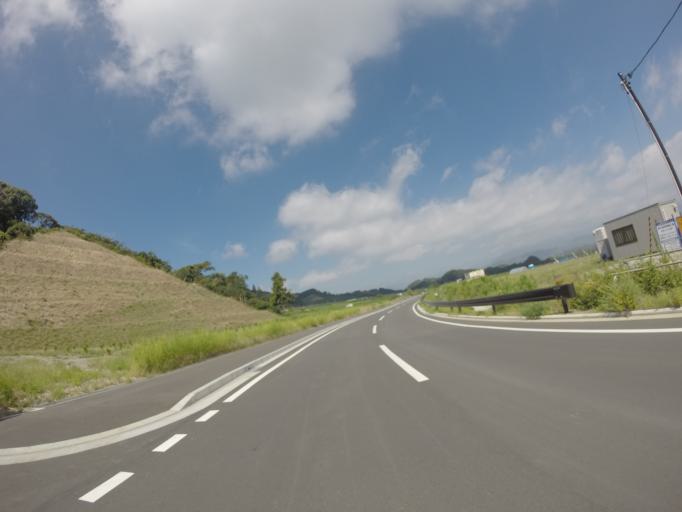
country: JP
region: Shizuoka
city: Shizuoka-shi
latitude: 34.9862
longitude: 138.4717
